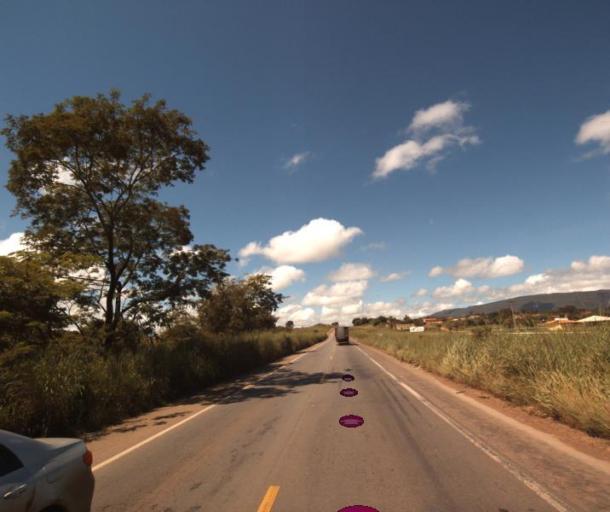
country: BR
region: Goias
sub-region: Jaragua
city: Jaragua
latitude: -15.7464
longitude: -49.3186
